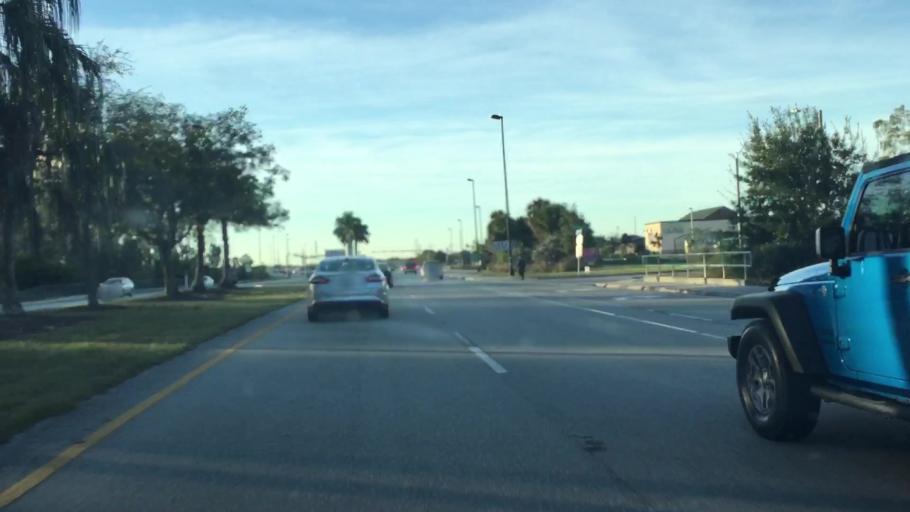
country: US
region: Florida
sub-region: Lee County
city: Three Oaks
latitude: 26.4959
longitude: -81.7837
